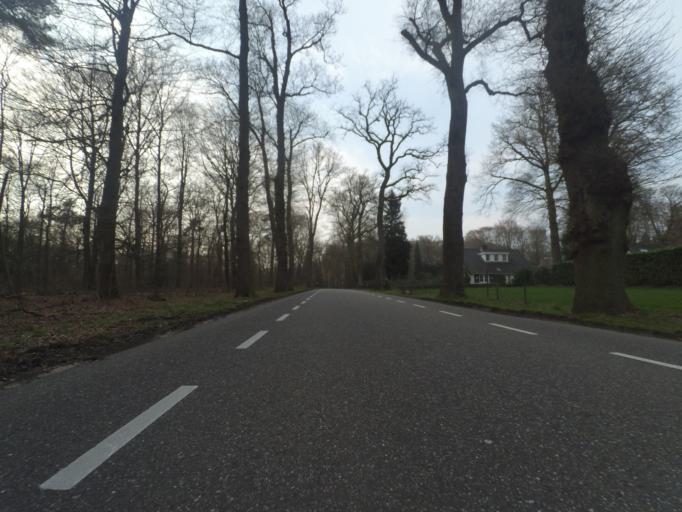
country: NL
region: Gelderland
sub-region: Gemeente Apeldoorn
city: Beekbergen
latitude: 52.1328
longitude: 5.8826
